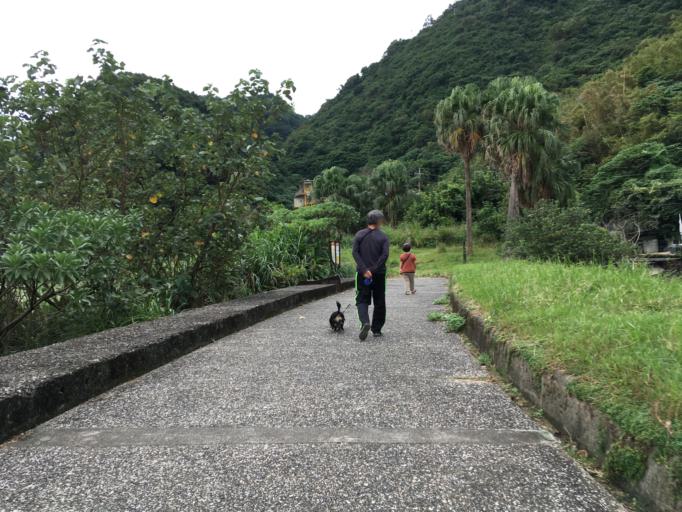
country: TW
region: Taiwan
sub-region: Yilan
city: Yilan
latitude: 24.5735
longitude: 121.8690
